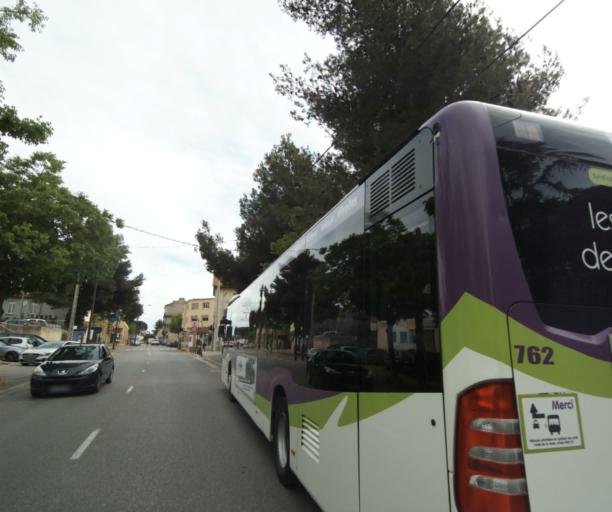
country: FR
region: Provence-Alpes-Cote d'Azur
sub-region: Departement des Bouches-du-Rhone
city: Rognac
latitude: 43.4888
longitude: 5.2299
